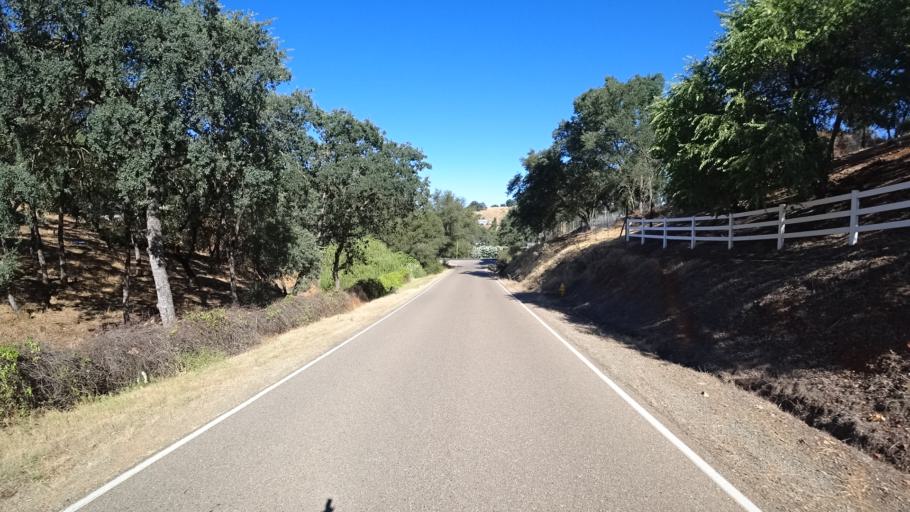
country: US
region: California
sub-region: Calaveras County
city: Rancho Calaveras
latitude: 38.1106
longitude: -120.8632
